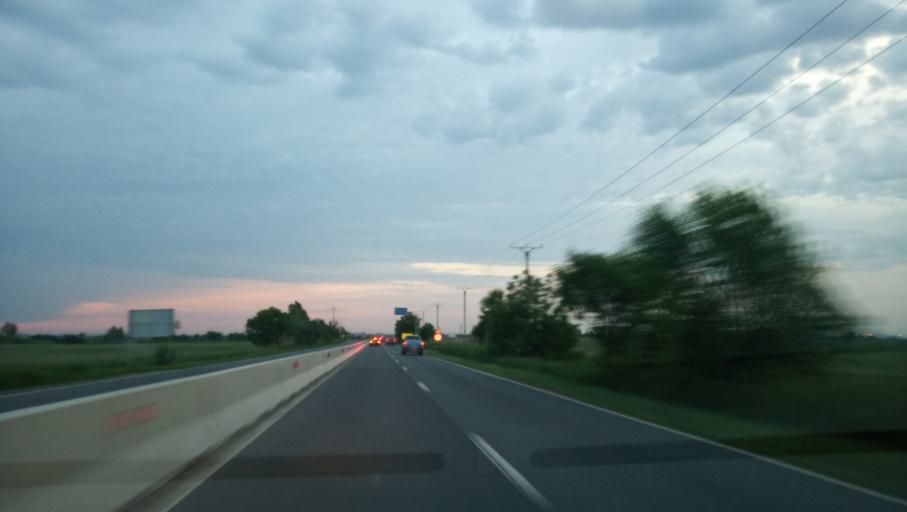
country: RO
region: Timis
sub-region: Comuna Sag
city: Sag
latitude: 45.6797
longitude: 21.1693
